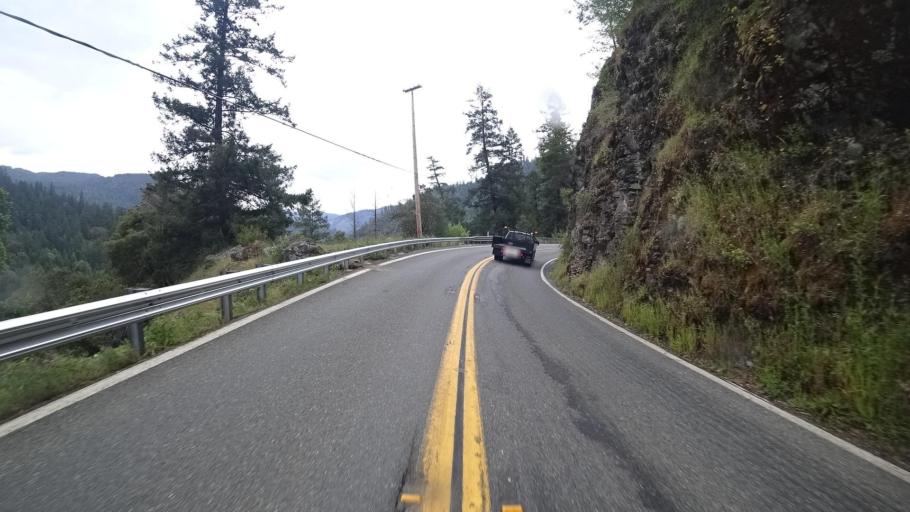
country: US
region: California
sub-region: Humboldt County
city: Willow Creek
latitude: 41.1217
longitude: -123.6876
